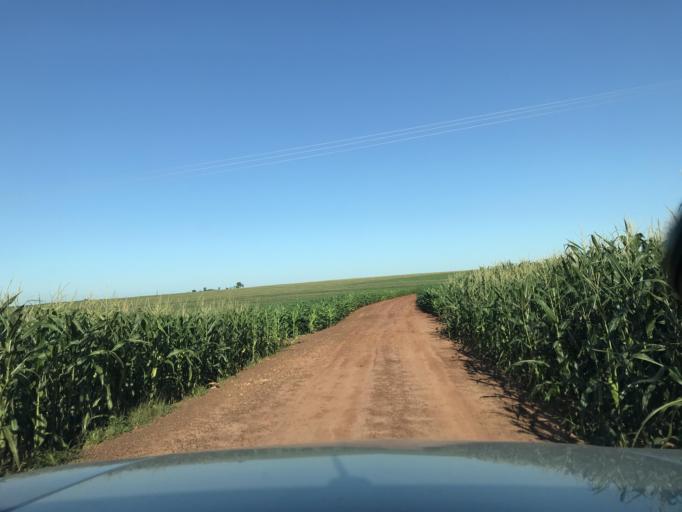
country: BR
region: Parana
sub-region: Palotina
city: Palotina
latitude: -24.2332
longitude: -53.7700
